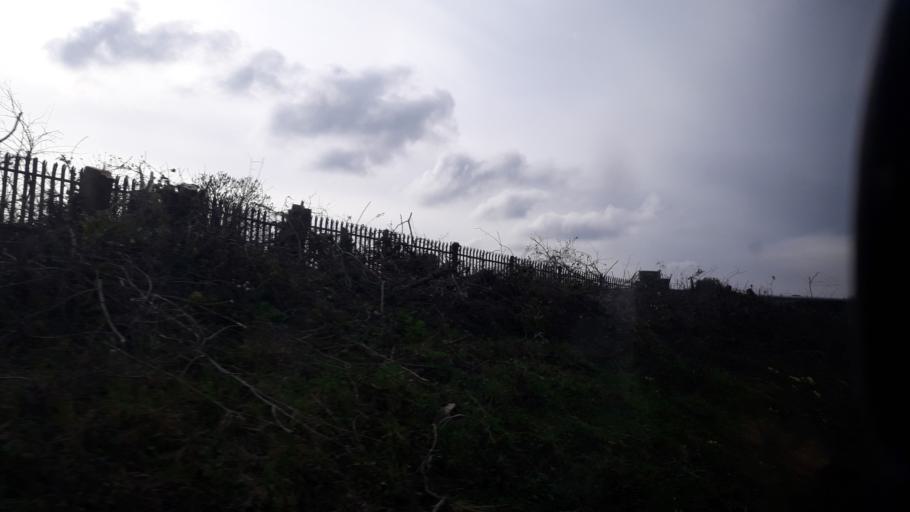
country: IE
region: Leinster
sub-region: Kildare
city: Kilcock
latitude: 53.4078
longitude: -6.6834
